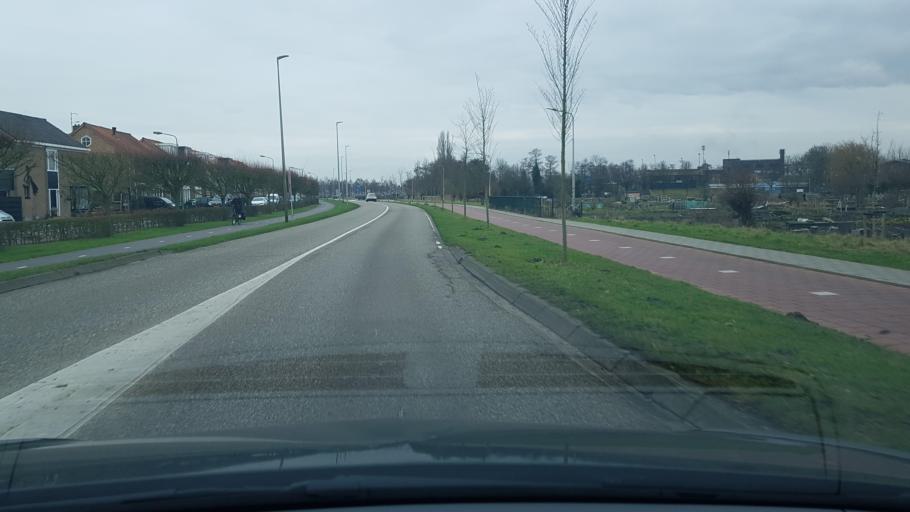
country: NL
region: North Holland
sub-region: Gemeente Uitgeest
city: Uitgeest
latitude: 52.5258
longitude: 4.7052
